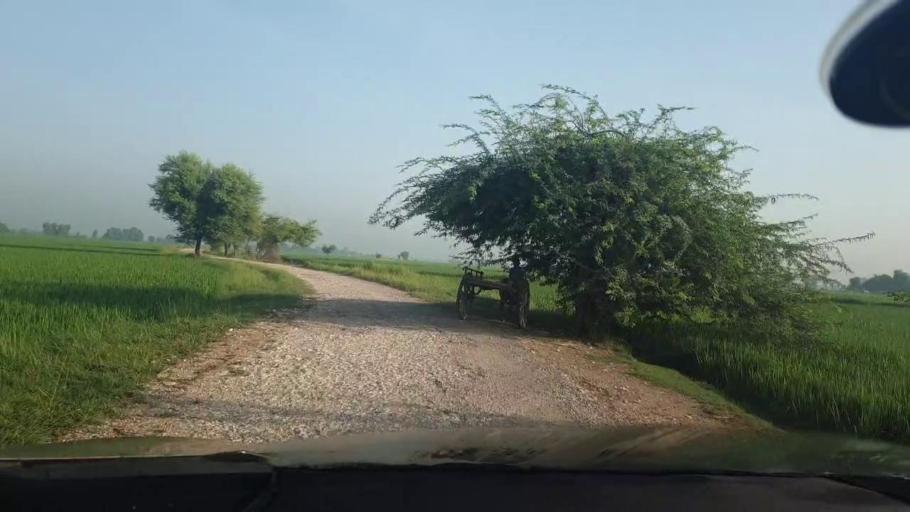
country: PK
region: Sindh
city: Kambar
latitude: 27.6202
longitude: 68.0186
